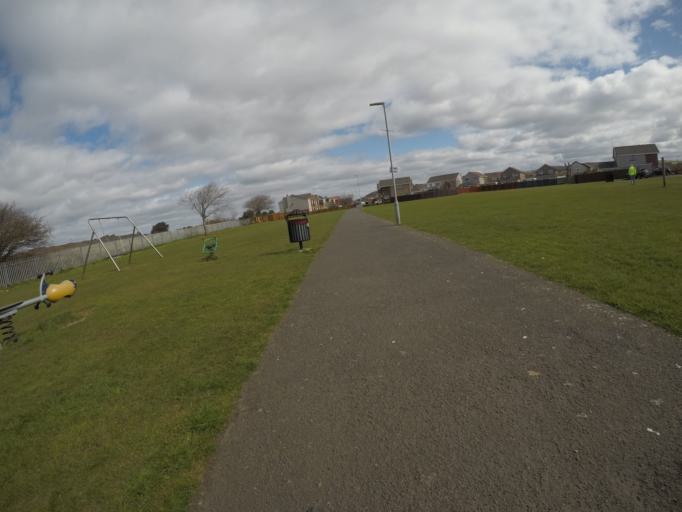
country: GB
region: Scotland
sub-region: South Ayrshire
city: Troon
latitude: 55.5624
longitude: -4.6490
